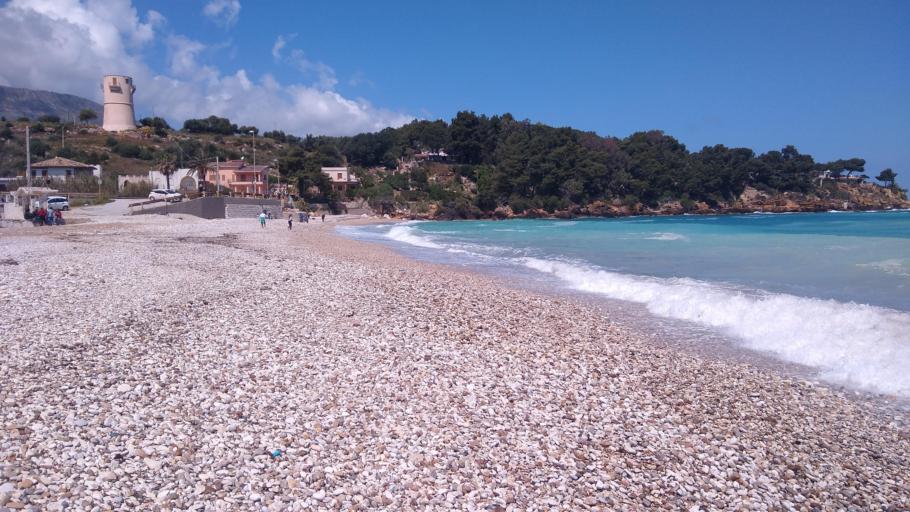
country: IT
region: Sicily
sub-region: Trapani
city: Castellammare del Golfo
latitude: 38.0568
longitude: 12.8400
